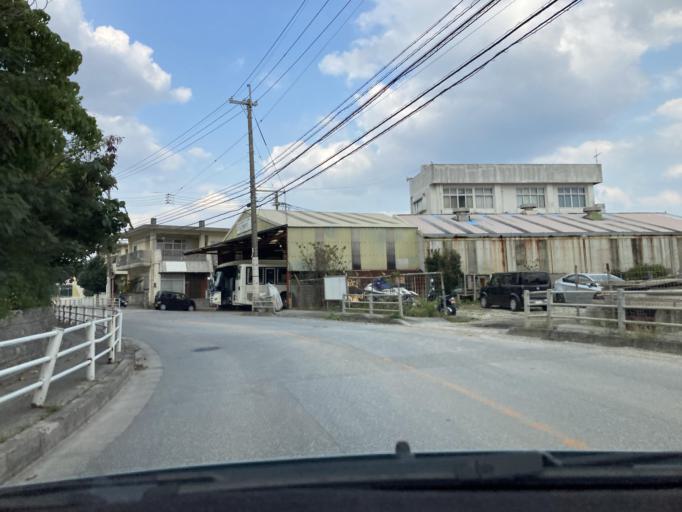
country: JP
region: Okinawa
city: Tomigusuku
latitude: 26.2001
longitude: 127.7346
